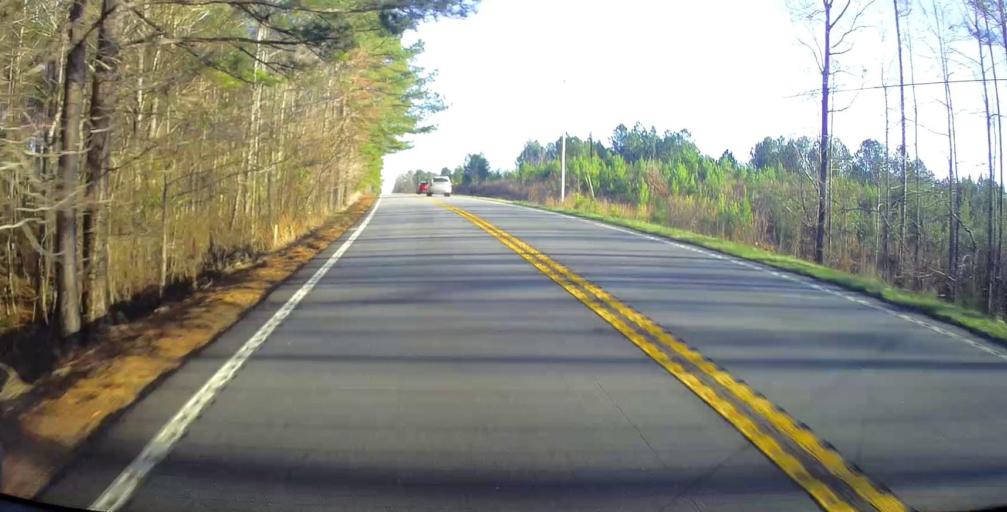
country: US
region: Alabama
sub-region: Chambers County
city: Valley
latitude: 32.7914
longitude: -85.1010
